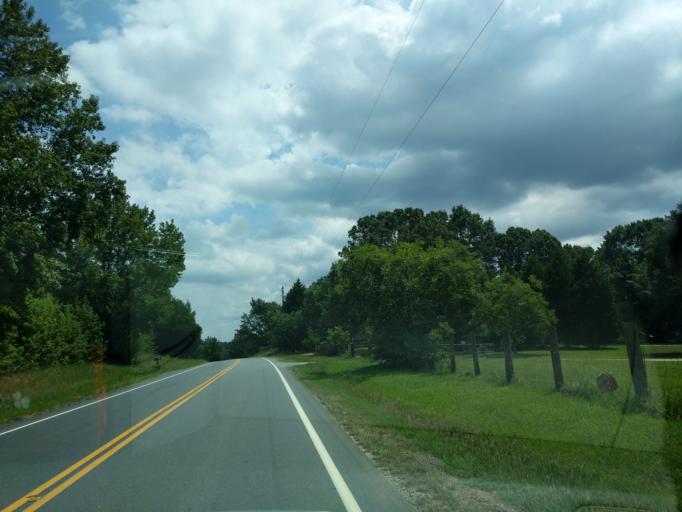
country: US
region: South Carolina
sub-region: Spartanburg County
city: Inman Mills
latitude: 34.9982
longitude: -82.1261
